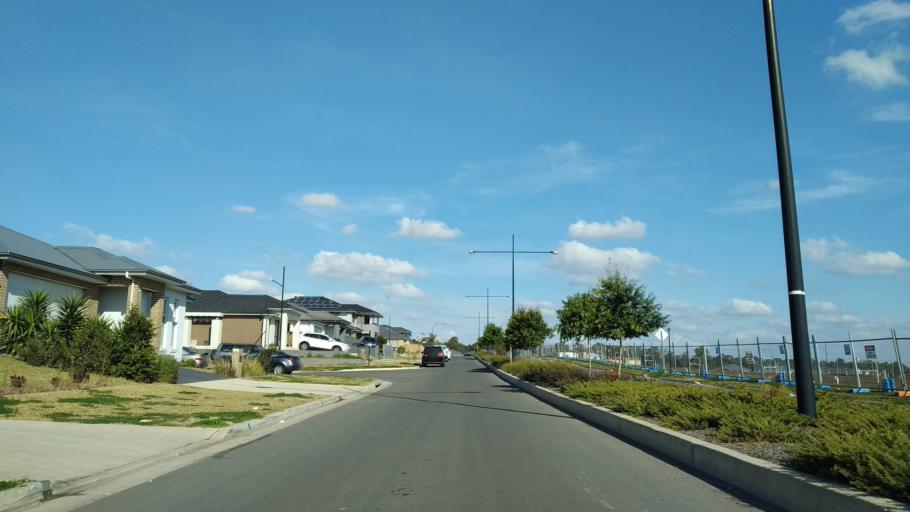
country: AU
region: New South Wales
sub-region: Blacktown
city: Hassall Grove
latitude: -33.7204
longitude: 150.8530
